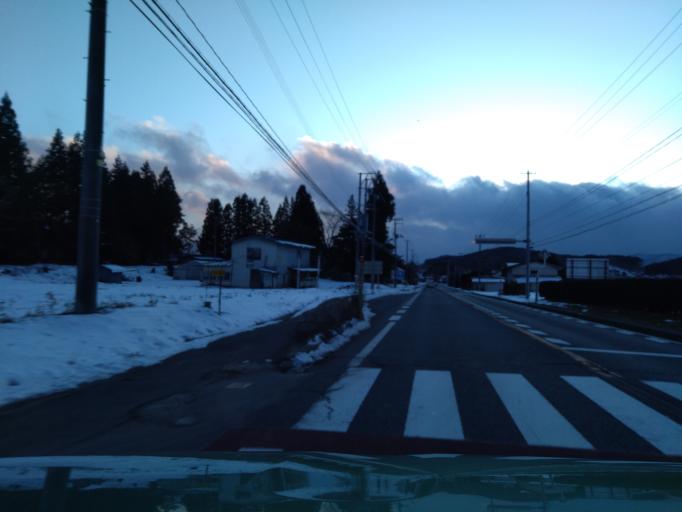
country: JP
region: Iwate
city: Shizukuishi
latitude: 39.6950
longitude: 141.0186
